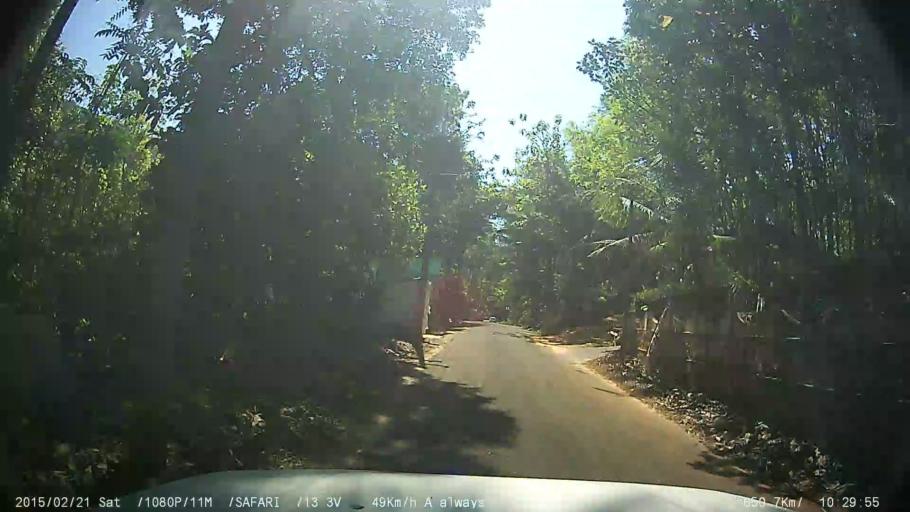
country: IN
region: Kerala
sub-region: Kottayam
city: Palackattumala
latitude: 9.8523
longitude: 76.6984
